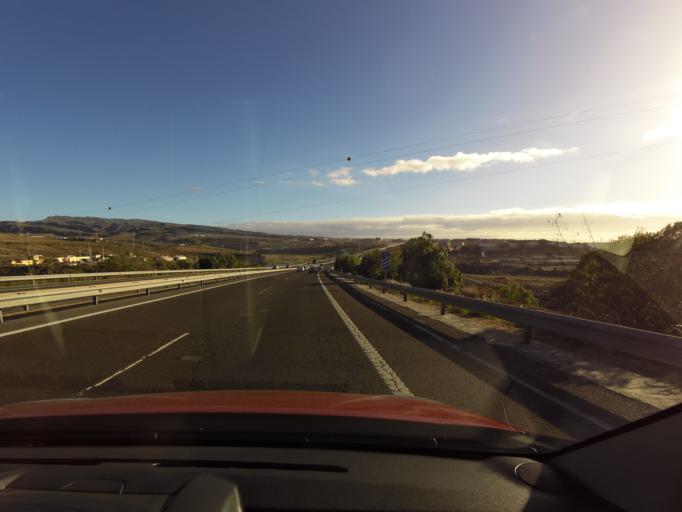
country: ES
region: Canary Islands
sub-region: Provincia de Las Palmas
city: Maspalomas
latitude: 27.7691
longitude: -15.5975
